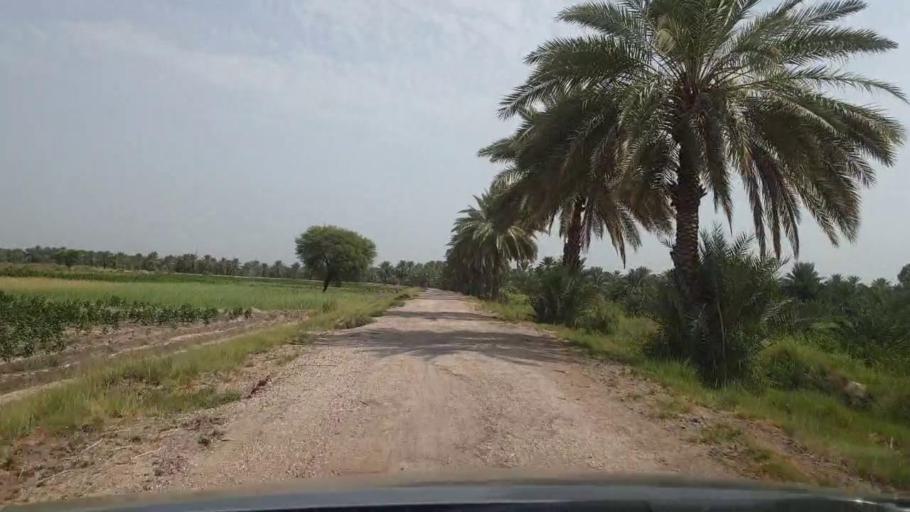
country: PK
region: Sindh
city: Rohri
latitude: 27.6829
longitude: 69.0359
